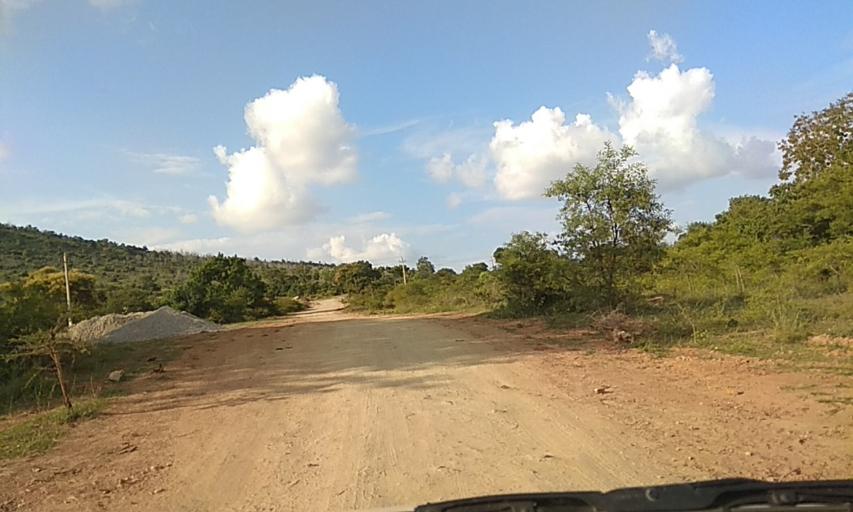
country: IN
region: Karnataka
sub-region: Chamrajnagar
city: Gundlupet
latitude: 11.7772
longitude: 76.7882
